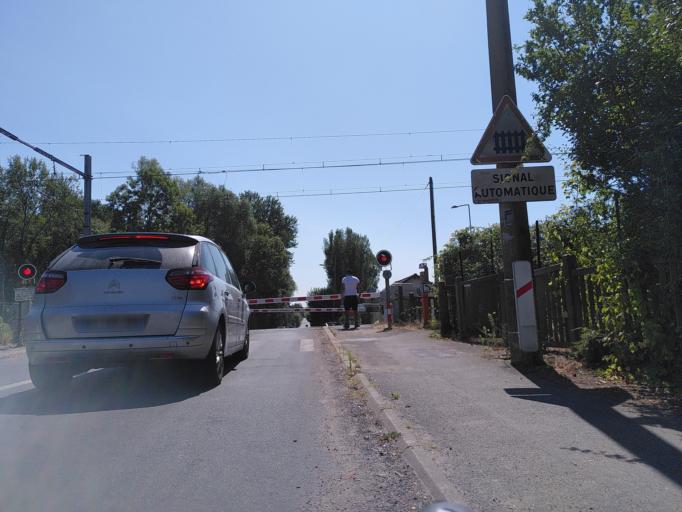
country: FR
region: Ile-de-France
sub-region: Departement de l'Essonne
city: Bruyeres-le-Chatel
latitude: 48.5785
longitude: 2.1937
